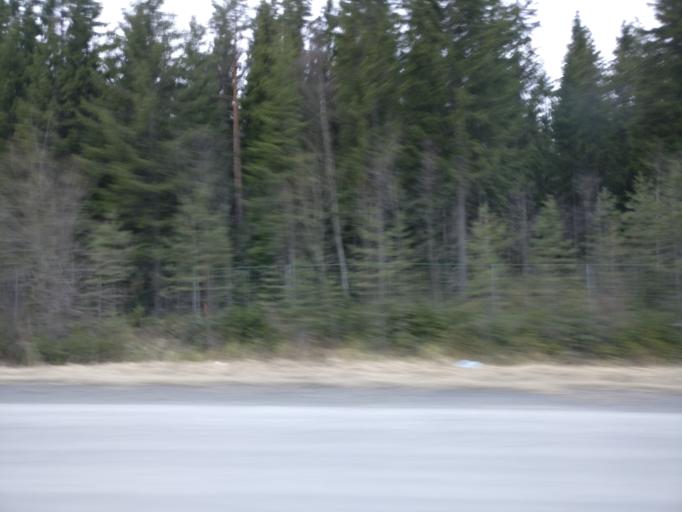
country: FI
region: Haeme
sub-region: Haemeenlinna
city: Kalvola
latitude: 61.1172
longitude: 24.1301
